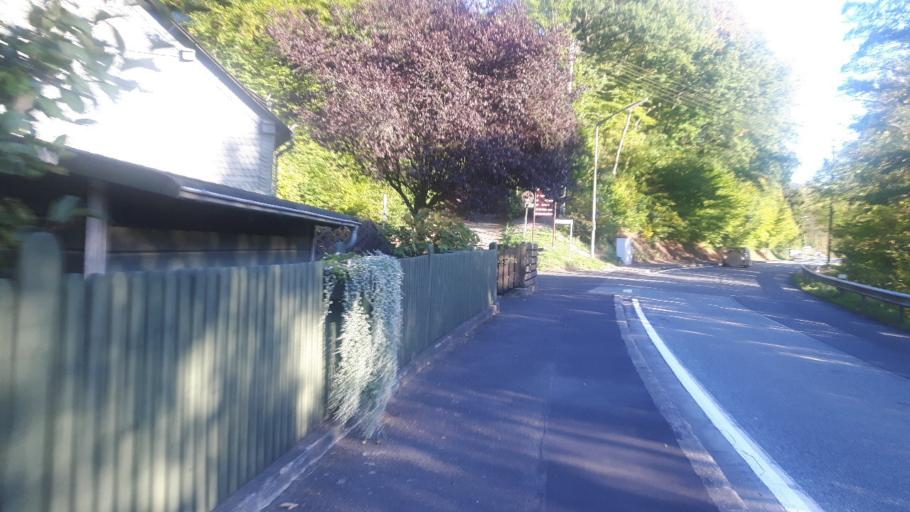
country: DE
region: Rheinland-Pfalz
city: Kirchen
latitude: 50.8237
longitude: 7.8861
